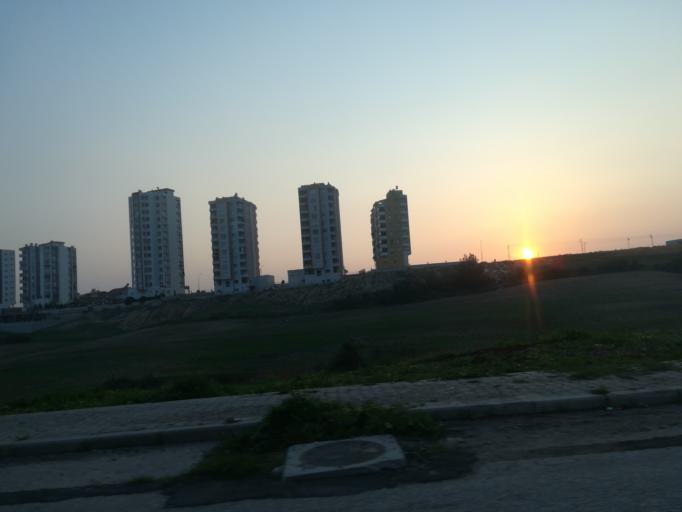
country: TR
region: Adana
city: Adana
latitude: 37.0802
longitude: 35.4120
